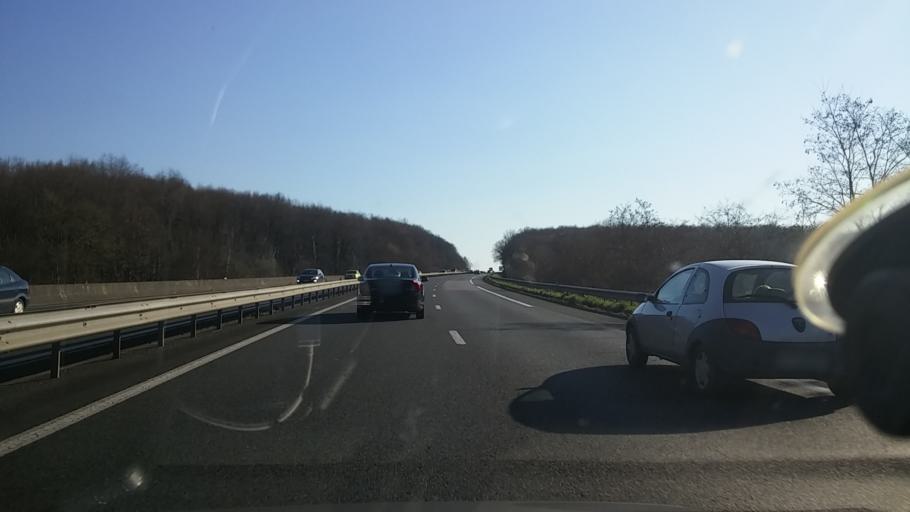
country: FR
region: Centre
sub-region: Departement de l'Indre
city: Saint-Marcel
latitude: 46.6261
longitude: 1.5480
